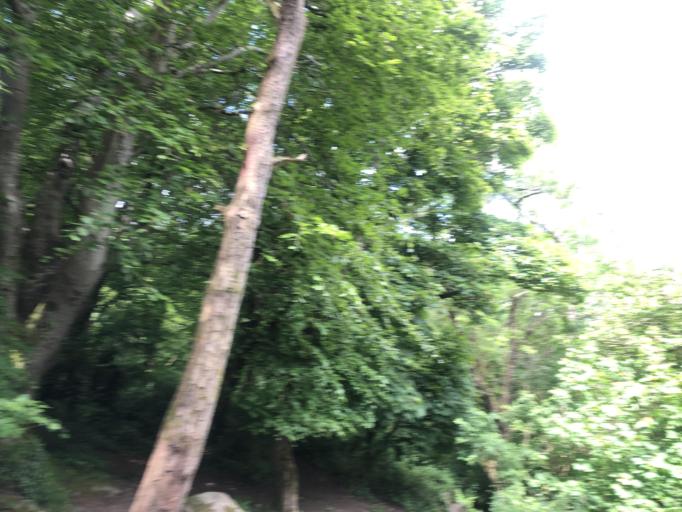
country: IE
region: Leinster
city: Dalkey
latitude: 53.2668
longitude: -6.1102
